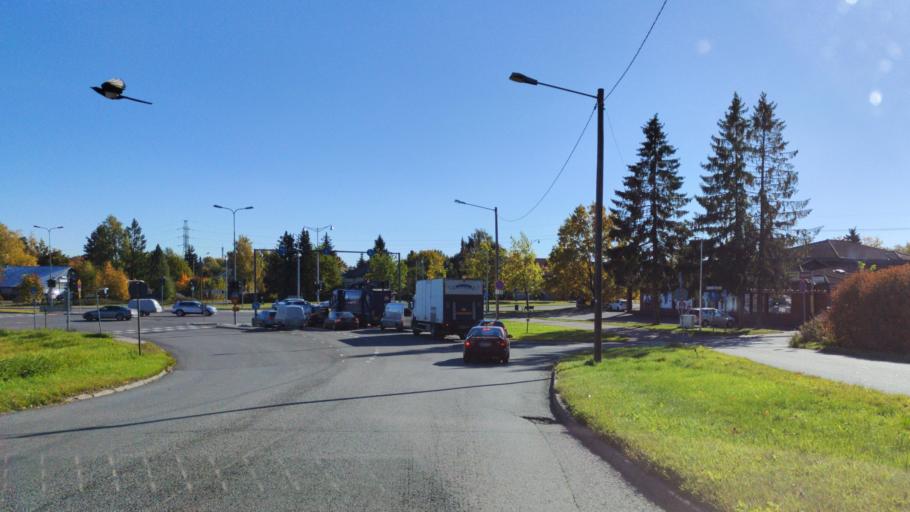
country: FI
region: Varsinais-Suomi
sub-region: Turku
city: Turku
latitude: 60.4728
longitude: 22.2817
